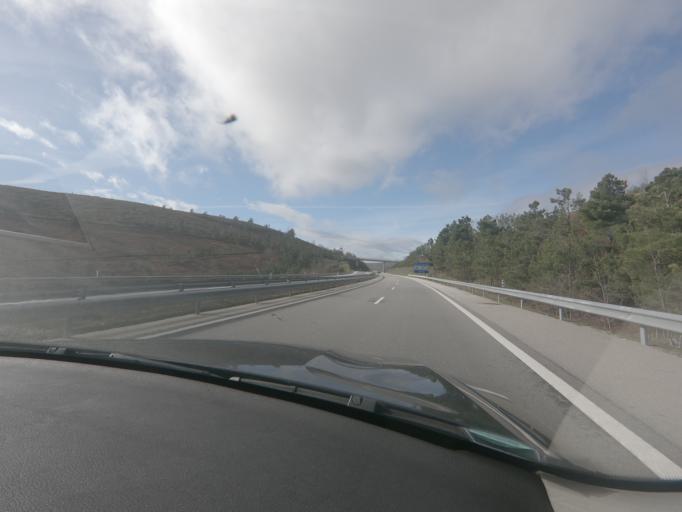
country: PT
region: Viseu
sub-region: Lamego
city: Lamego
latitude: 41.0490
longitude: -7.8494
